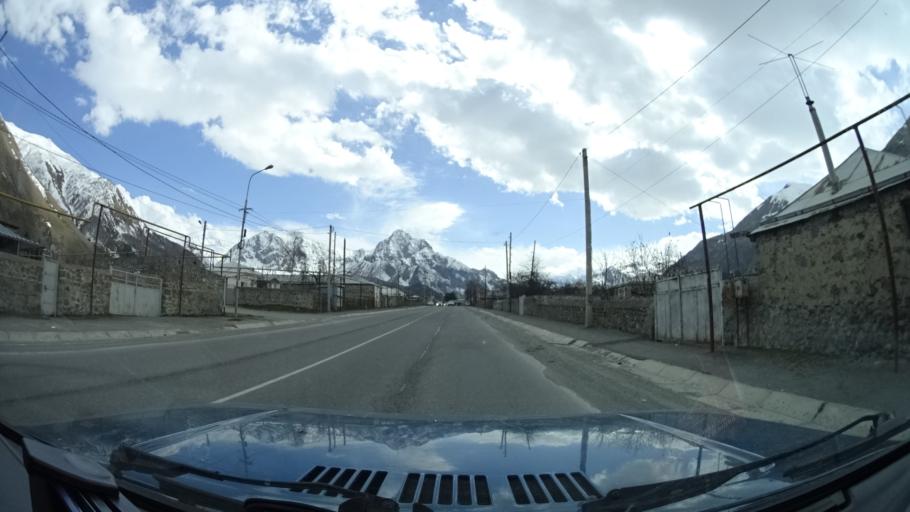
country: GE
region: Mtskheta-Mtianeti
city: Step'antsminda
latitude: 42.6158
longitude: 44.5965
